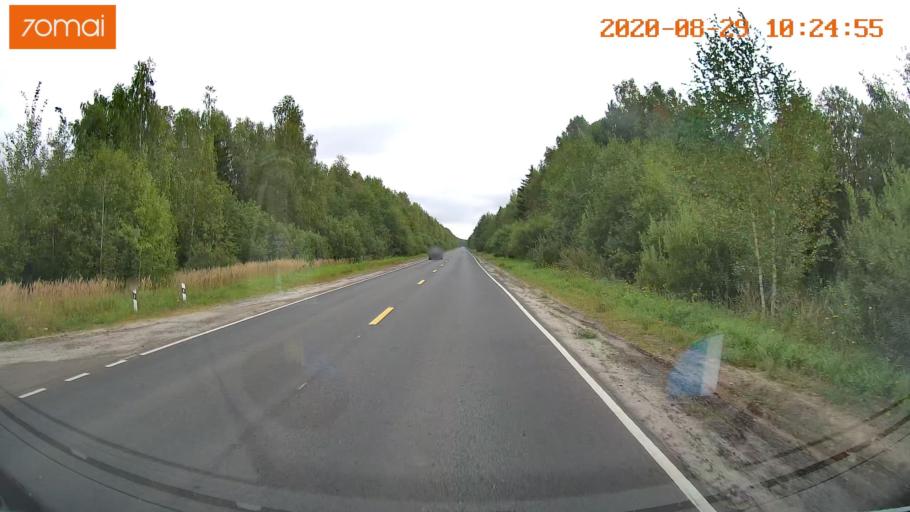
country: RU
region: Ivanovo
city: Yur'yevets
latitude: 57.3198
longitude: 43.0097
